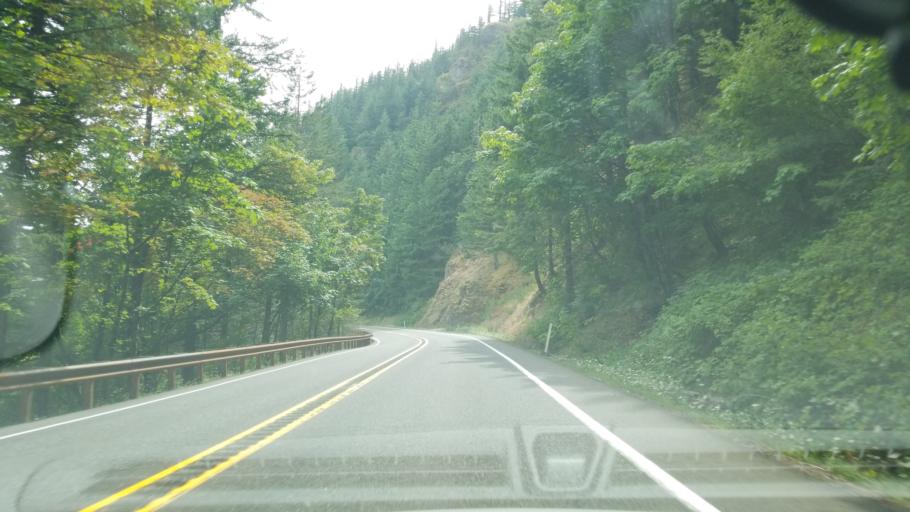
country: US
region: Washington
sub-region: Clark County
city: Washougal
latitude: 45.5836
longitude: -122.1940
